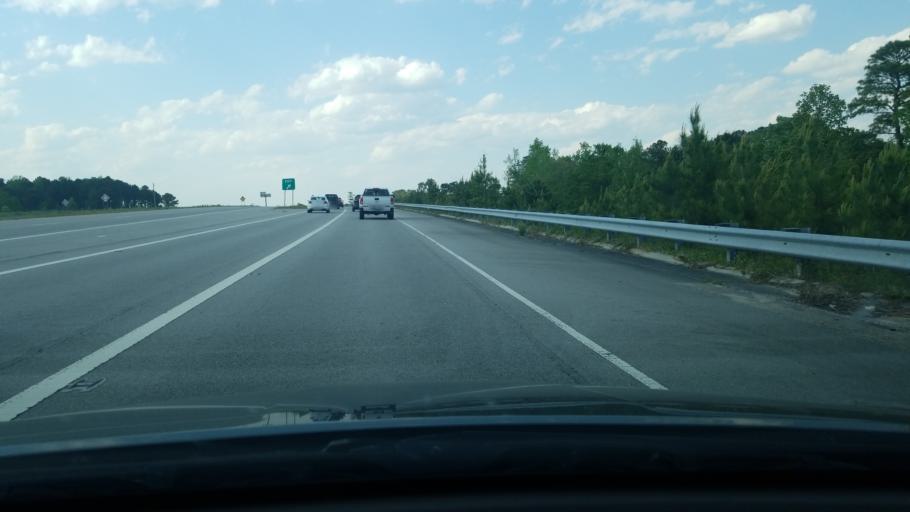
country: US
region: North Carolina
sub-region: Onslow County
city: Pumpkin Center
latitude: 34.7661
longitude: -77.3955
